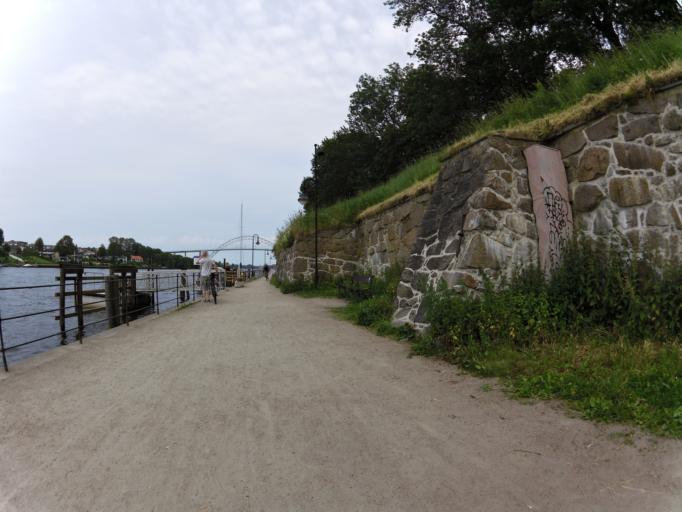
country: NO
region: Ostfold
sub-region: Fredrikstad
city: Fredrikstad
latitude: 59.2052
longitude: 10.9536
